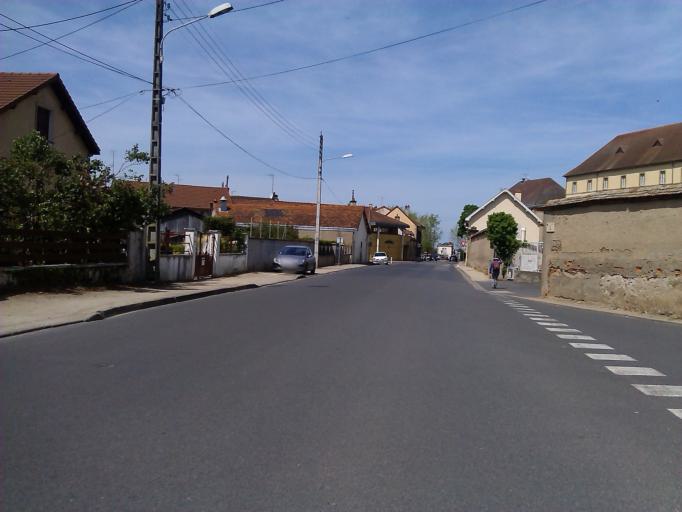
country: FR
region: Auvergne
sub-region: Departement de l'Allier
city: Yzeure
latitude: 46.5656
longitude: 3.3564
